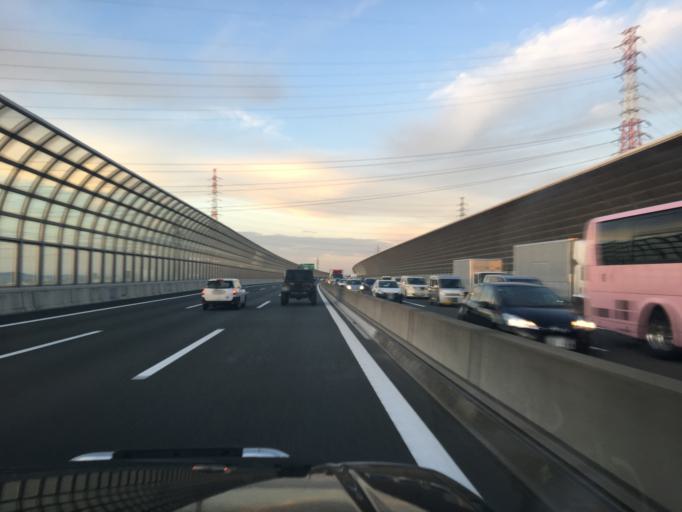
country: JP
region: Osaka
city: Daitocho
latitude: 34.7351
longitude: 135.6099
